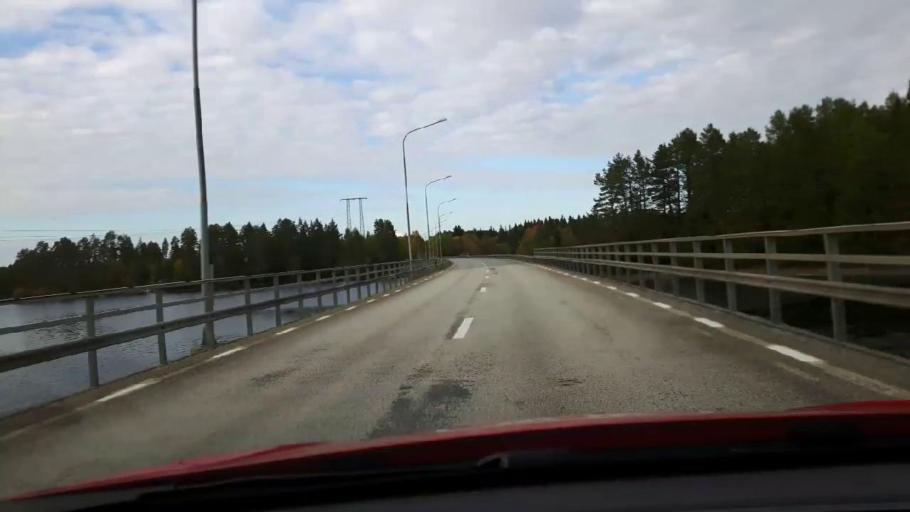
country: SE
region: Jaemtland
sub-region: Krokoms Kommun
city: Valla
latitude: 63.2510
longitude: 13.9986
